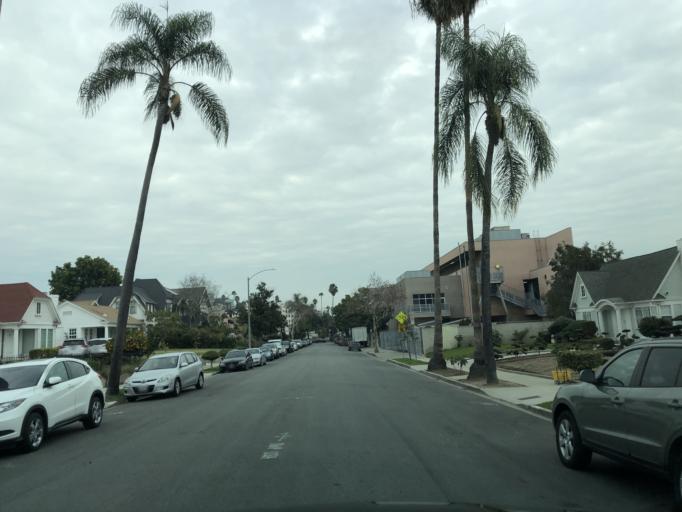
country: US
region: California
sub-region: Los Angeles County
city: Hollywood
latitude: 34.0590
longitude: -118.3168
